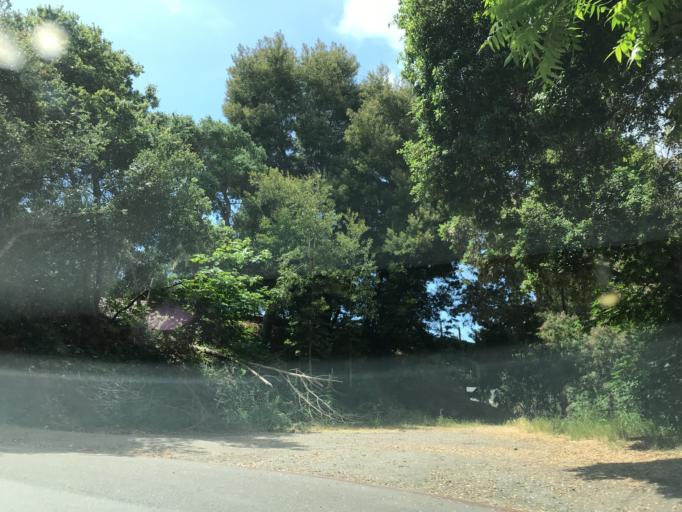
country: US
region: California
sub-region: Santa Cruz County
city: Aptos
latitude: 36.9771
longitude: -121.9034
